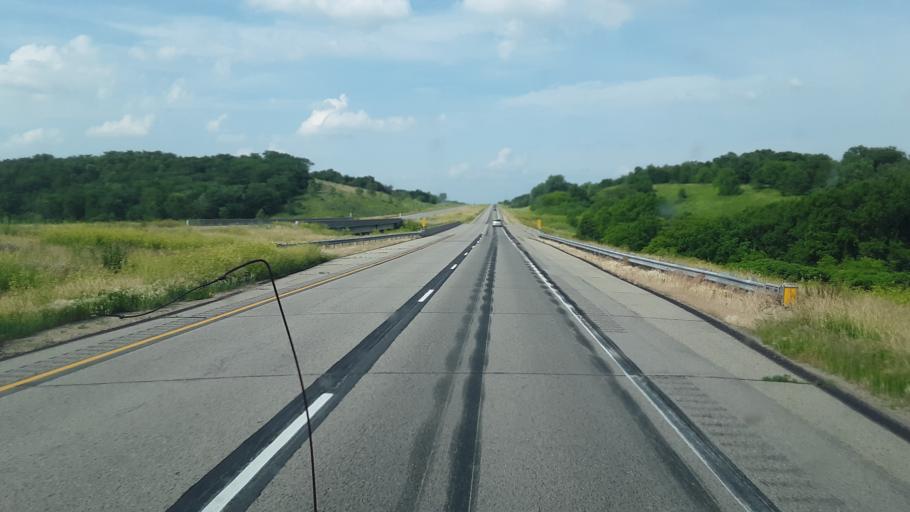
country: US
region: Iowa
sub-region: Jasper County
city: Baxter
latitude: 41.8539
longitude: -93.2462
